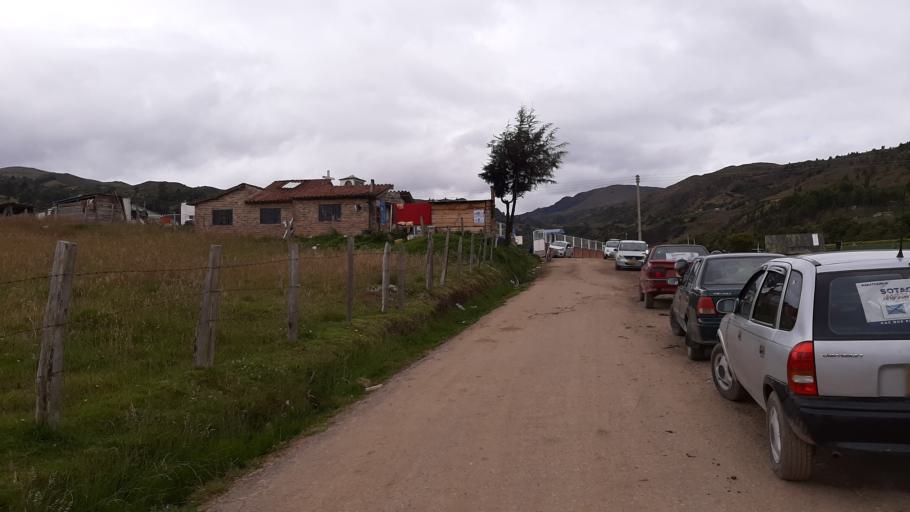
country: CO
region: Boyaca
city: Aquitania
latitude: 5.4811
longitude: -72.9461
